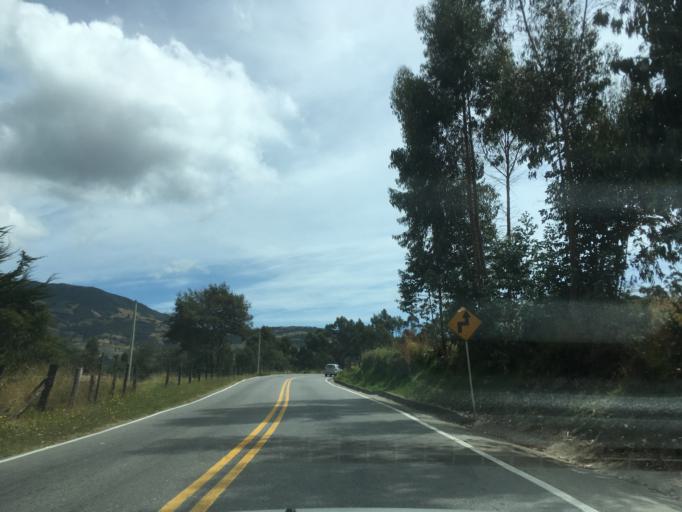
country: CO
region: Boyaca
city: Firavitoba
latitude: 5.6238
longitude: -72.9169
